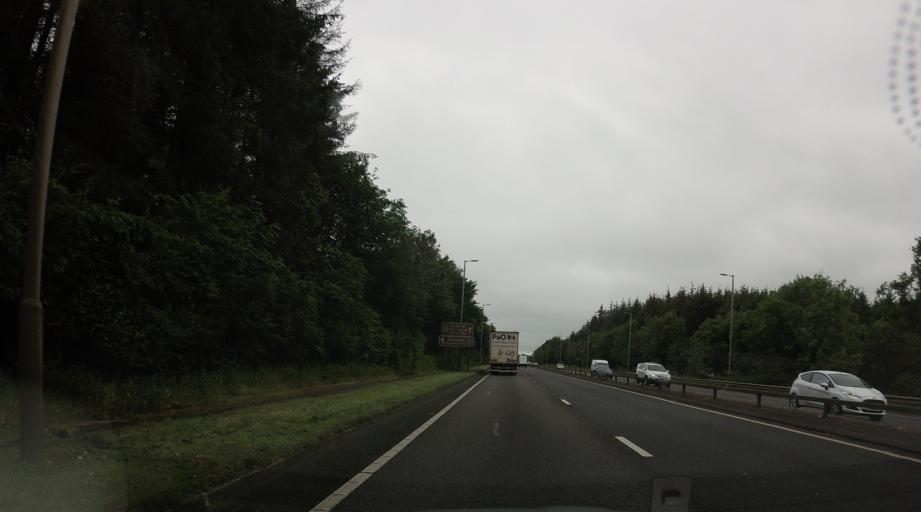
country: GB
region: Scotland
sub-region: South Lanarkshire
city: East Kilbride
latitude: 55.7810
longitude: -4.1438
